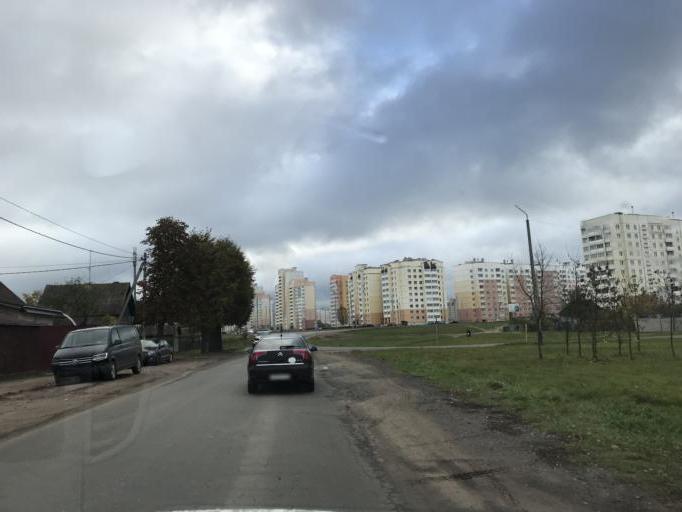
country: BY
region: Mogilev
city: Mahilyow
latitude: 53.8832
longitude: 30.3539
